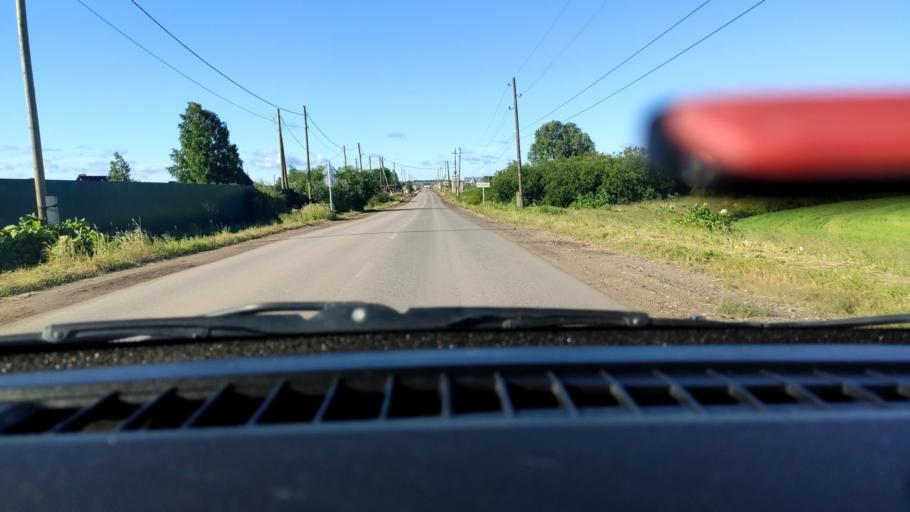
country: RU
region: Perm
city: Kultayevo
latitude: 57.8745
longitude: 55.9194
